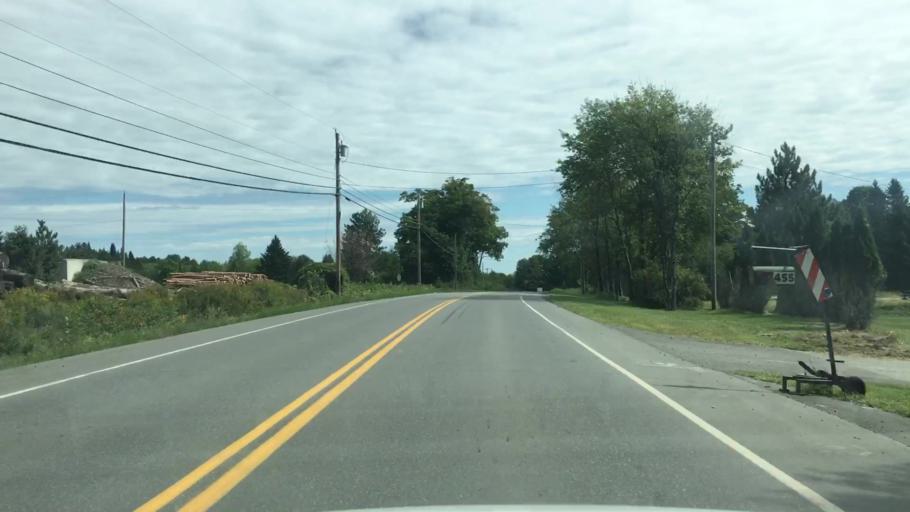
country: US
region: Maine
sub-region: Piscataquis County
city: Dover-Foxcroft
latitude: 45.2014
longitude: -69.1934
